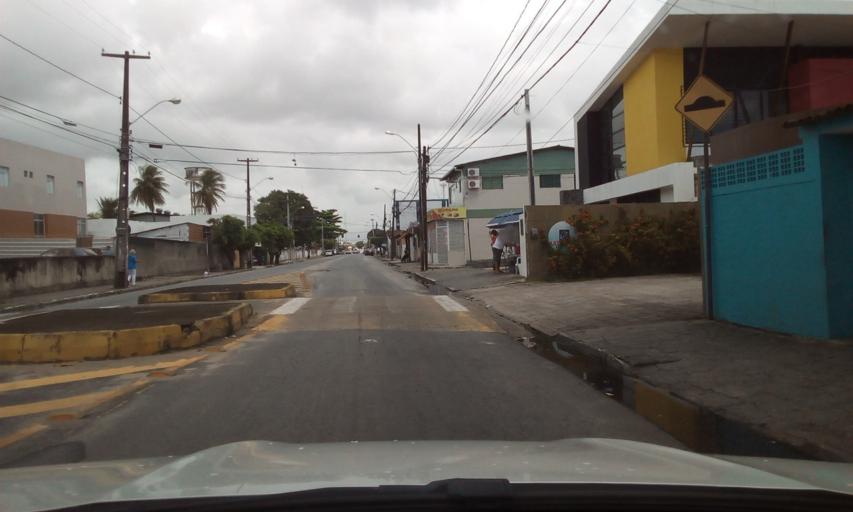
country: BR
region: Paraiba
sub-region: Joao Pessoa
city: Joao Pessoa
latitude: -7.1302
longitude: -34.8723
